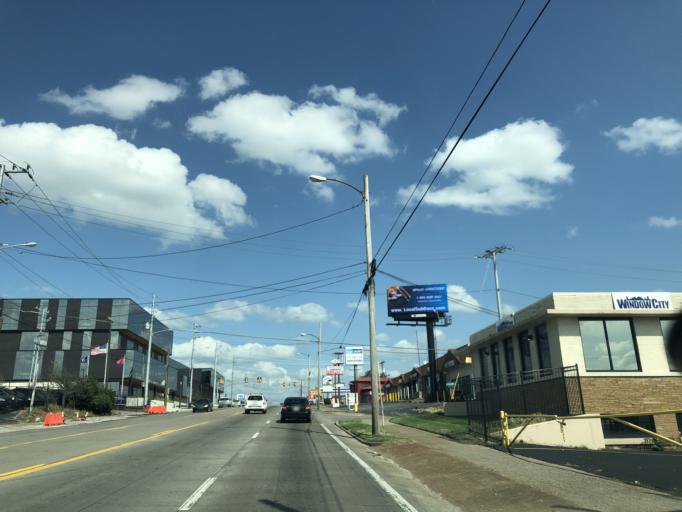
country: US
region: Tennessee
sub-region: Davidson County
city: Nashville
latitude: 36.1421
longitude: -86.7423
